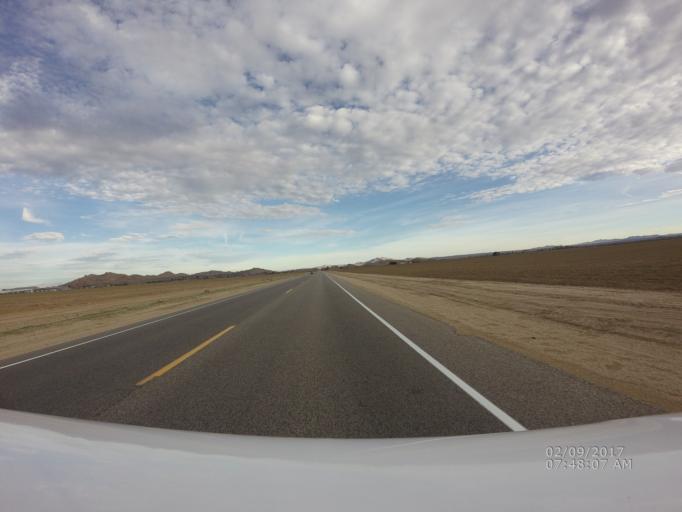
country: US
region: California
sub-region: Los Angeles County
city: Lake Los Angeles
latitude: 34.5660
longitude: -117.8265
